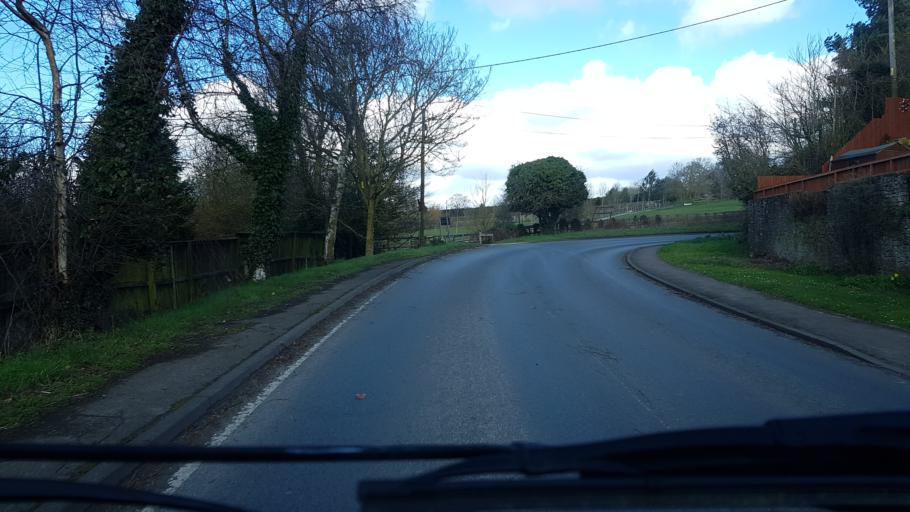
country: GB
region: England
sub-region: Wiltshire
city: Market Lavington
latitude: 51.2974
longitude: -1.9706
